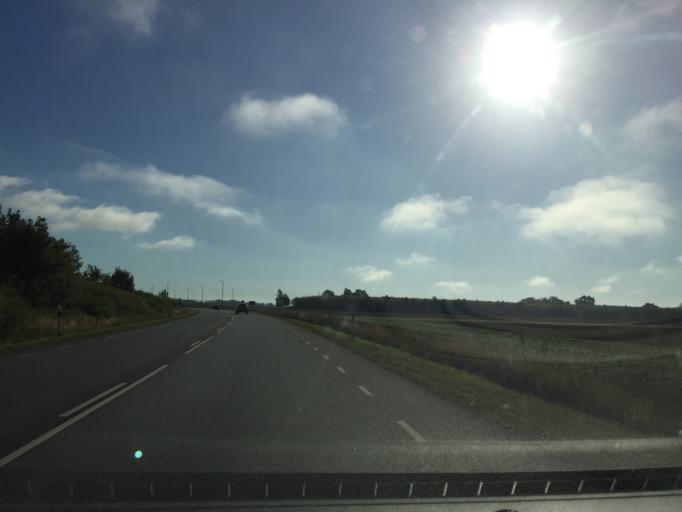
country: SE
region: Skane
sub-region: Staffanstorps Kommun
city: Hjaerup
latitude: 55.6811
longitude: 13.1671
